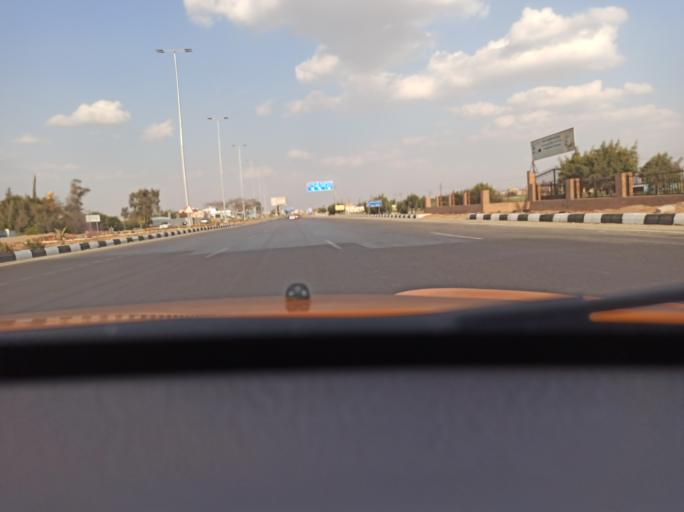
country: EG
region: Al Isma'iliyah
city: Ismailia
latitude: 30.6188
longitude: 32.2369
